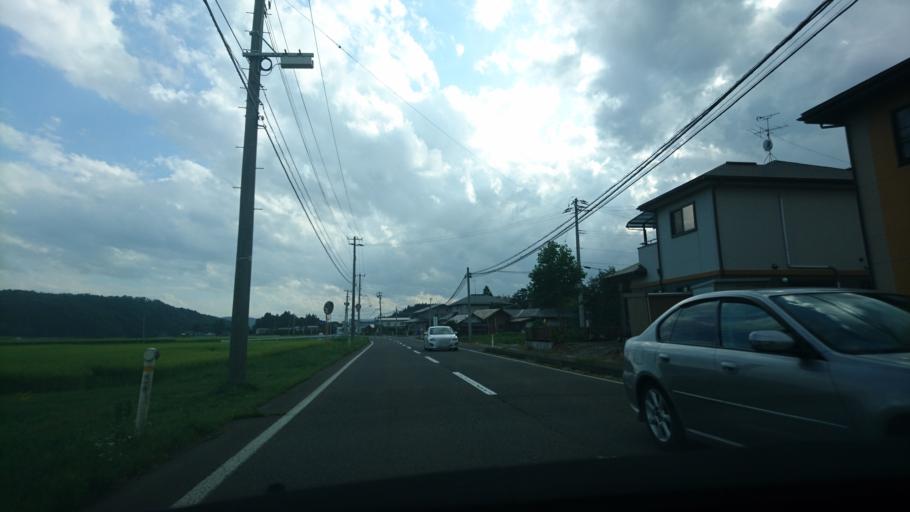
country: JP
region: Iwate
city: Kitakami
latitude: 39.3069
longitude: 141.1537
